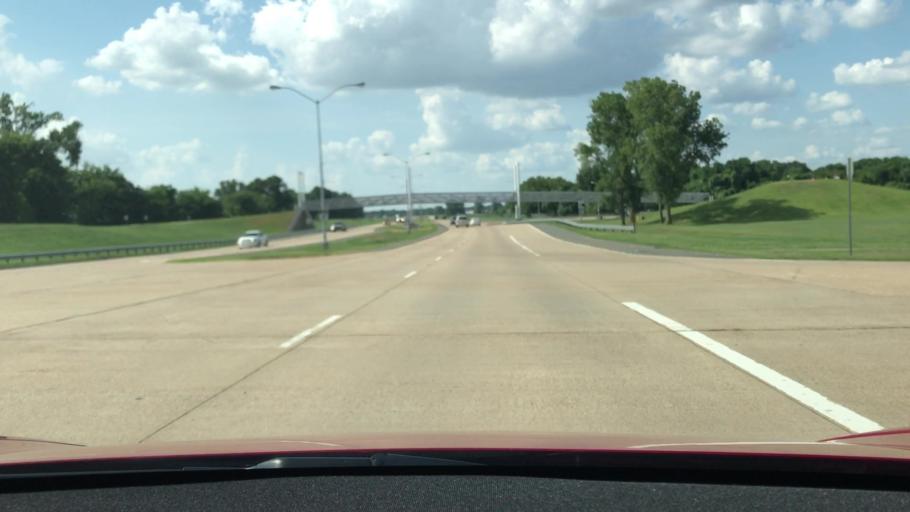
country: US
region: Louisiana
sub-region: Bossier Parish
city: Bossier City
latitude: 32.4674
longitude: -93.6771
